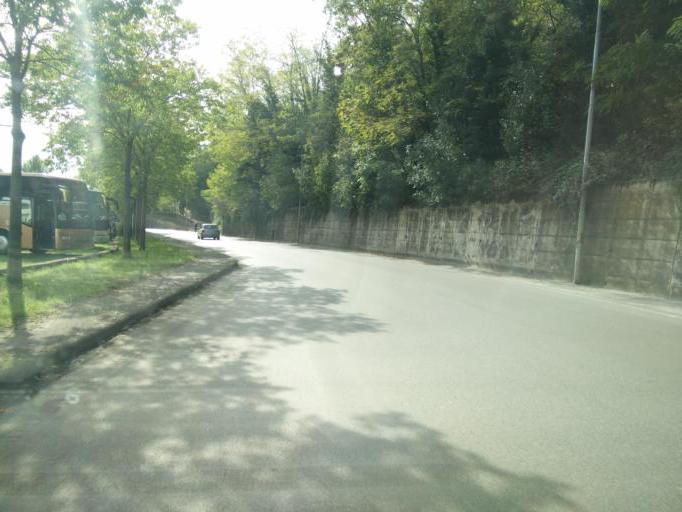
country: IT
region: Tuscany
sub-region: Provincia di Siena
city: Siena
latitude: 43.3162
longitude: 11.3163
